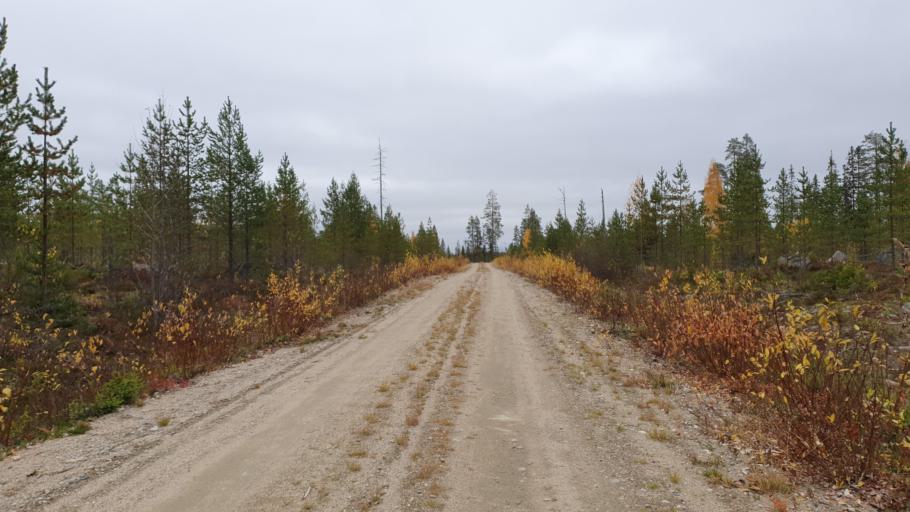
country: FI
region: Kainuu
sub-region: Kehys-Kainuu
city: Kuhmo
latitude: 64.4401
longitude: 29.6210
